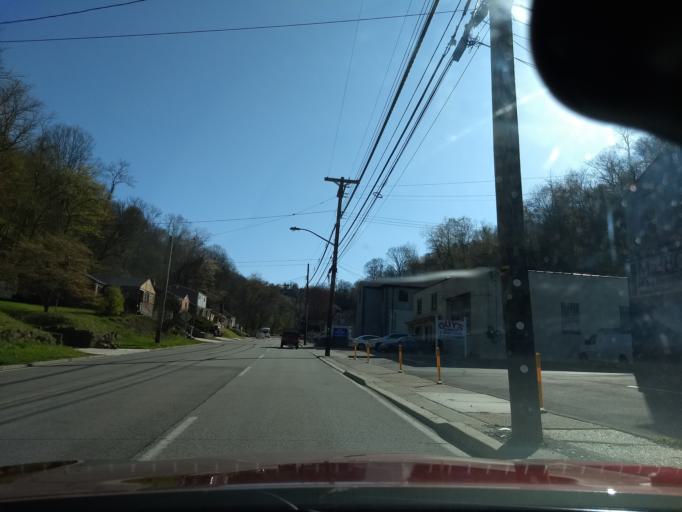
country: US
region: Pennsylvania
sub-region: Allegheny County
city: Mount Oliver
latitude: 40.4091
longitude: -79.9639
